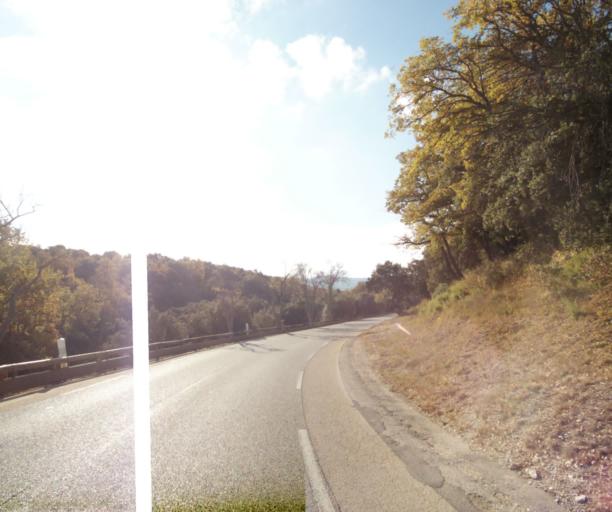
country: FR
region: Provence-Alpes-Cote d'Azur
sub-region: Departement des Bouches-du-Rhone
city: Cadolive
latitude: 43.3772
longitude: 5.5391
